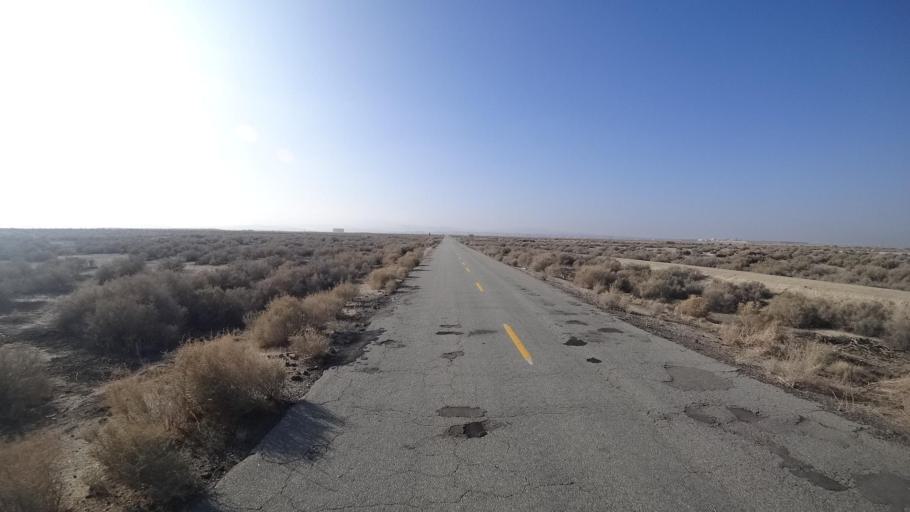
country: US
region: California
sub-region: Kern County
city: Maricopa
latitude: 35.1011
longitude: -119.3803
